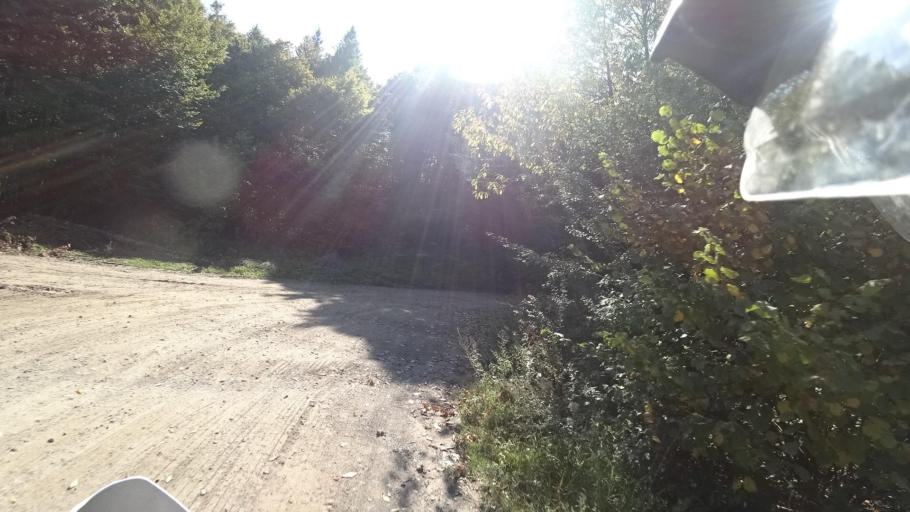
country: HR
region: Karlovacka
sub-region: Grad Ogulin
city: Ogulin
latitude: 45.2110
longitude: 15.1305
